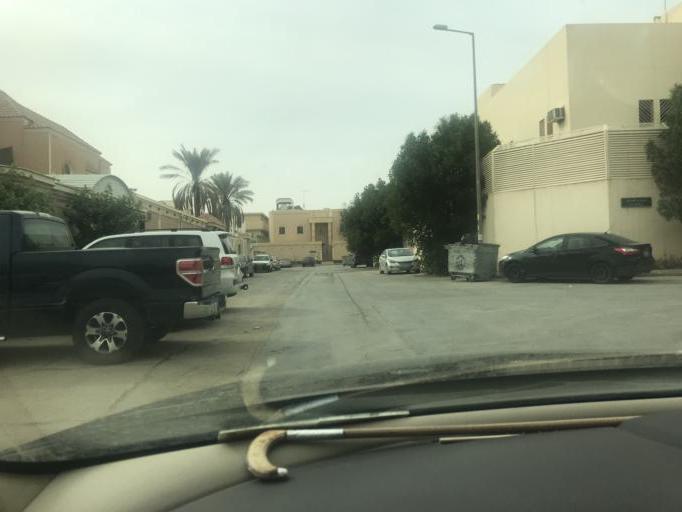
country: SA
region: Ar Riyad
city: Riyadh
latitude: 24.7552
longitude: 46.7666
